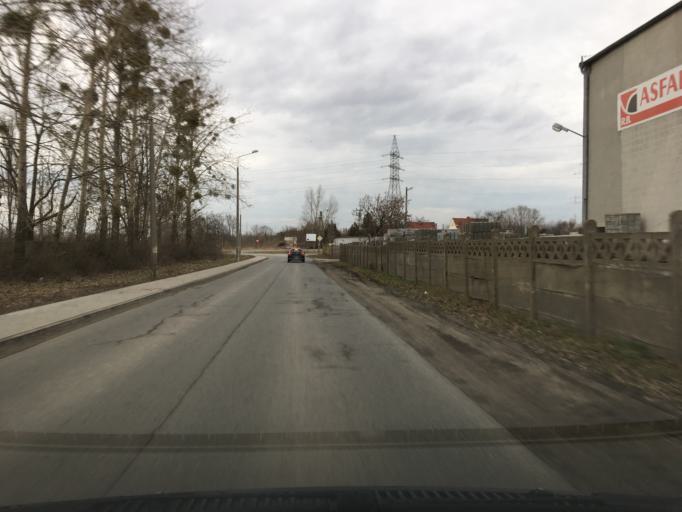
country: PL
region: Opole Voivodeship
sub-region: Powiat kedzierzynsko-kozielski
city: Kozle
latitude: 50.3509
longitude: 18.1413
